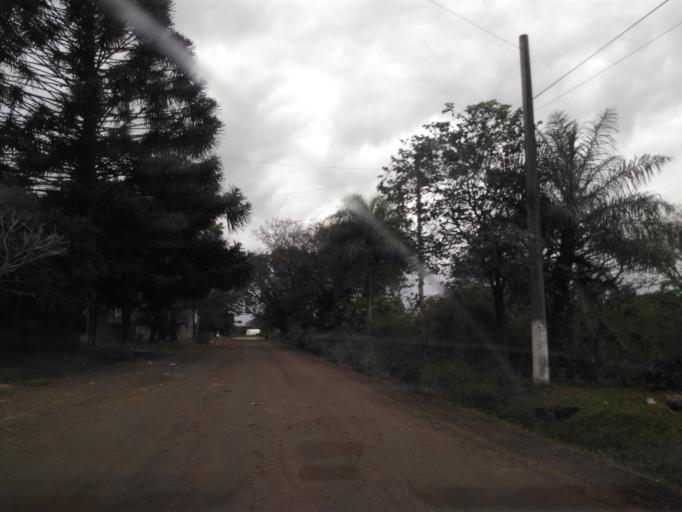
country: AR
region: Chaco
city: Fontana
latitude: -27.4295
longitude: -59.0143
